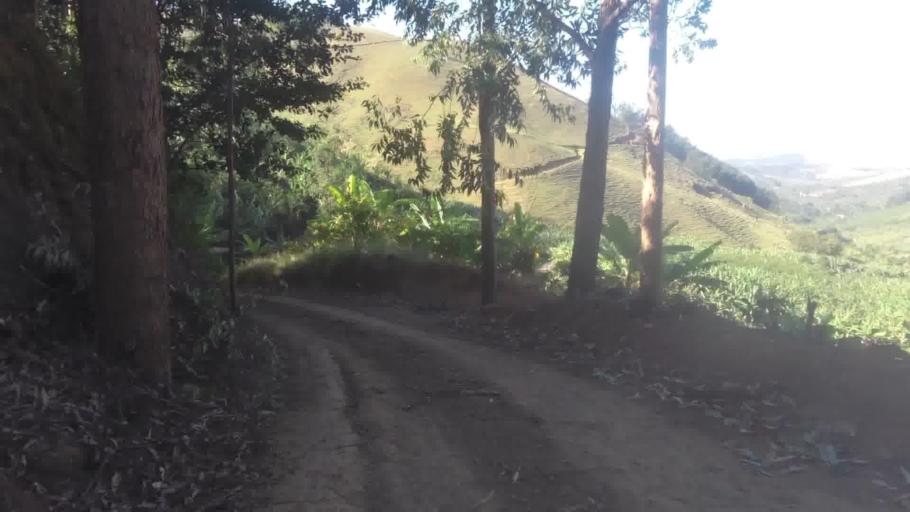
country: BR
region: Espirito Santo
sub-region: Iconha
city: Iconha
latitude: -20.7509
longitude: -40.8053
